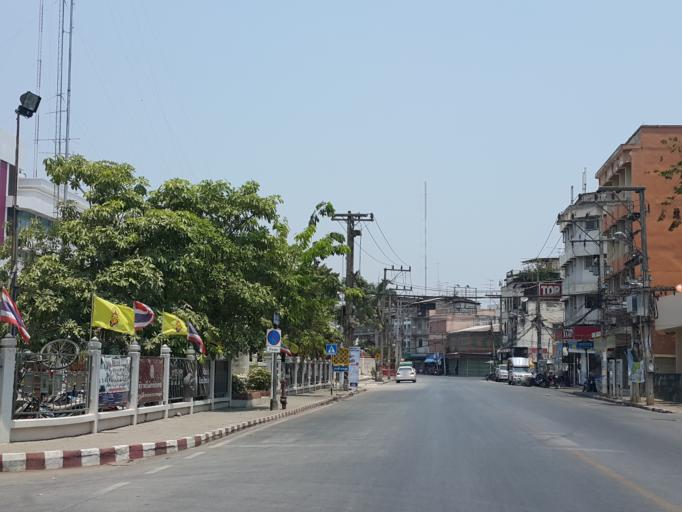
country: TH
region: Phitsanulok
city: Phitsanulok
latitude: 16.8156
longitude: 100.2629
